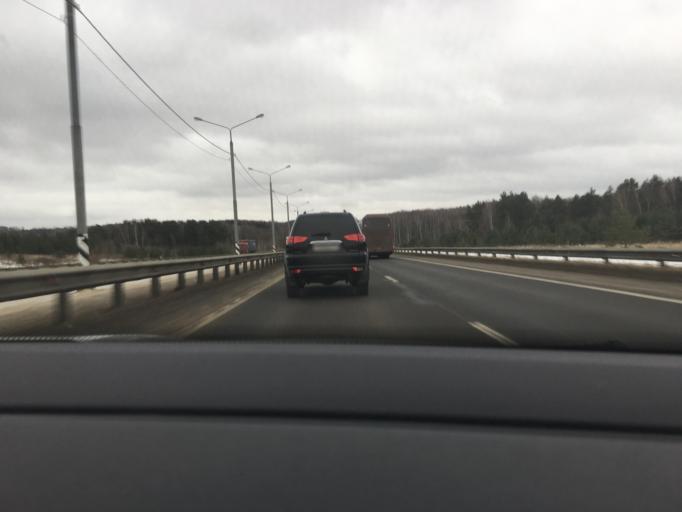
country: RU
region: Moskovskaya
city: Serpukhov
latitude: 54.8222
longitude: 37.4721
